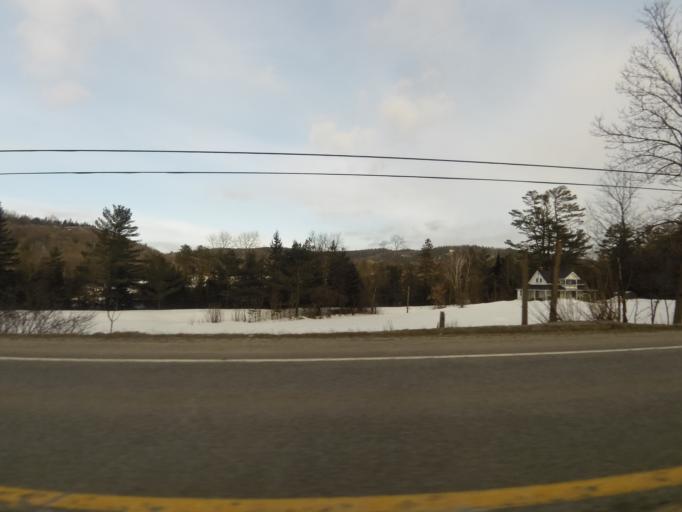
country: CA
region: Quebec
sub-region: Outaouais
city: Wakefield
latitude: 45.7652
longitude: -75.9319
